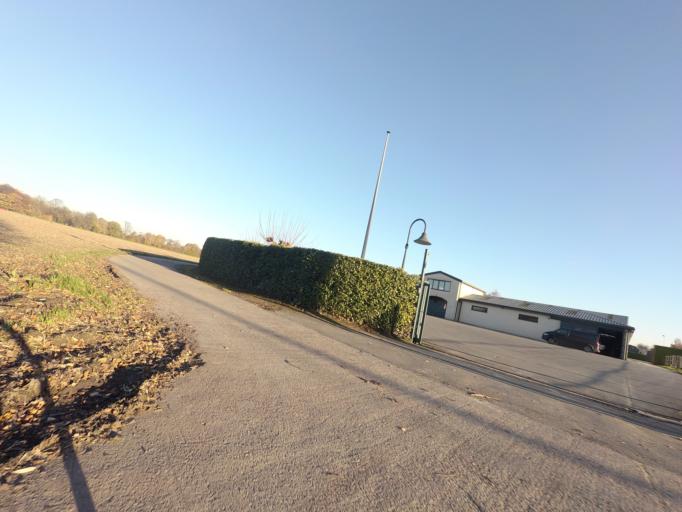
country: BE
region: Flanders
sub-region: Provincie Vlaams-Brabant
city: Zemst
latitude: 50.9797
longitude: 4.4327
